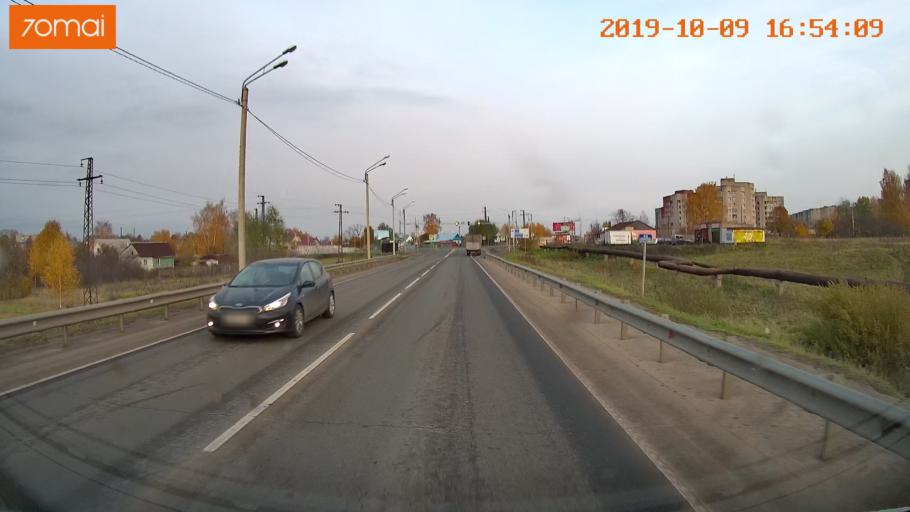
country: RU
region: Ivanovo
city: Privolzhsk
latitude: 57.3757
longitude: 41.2783
